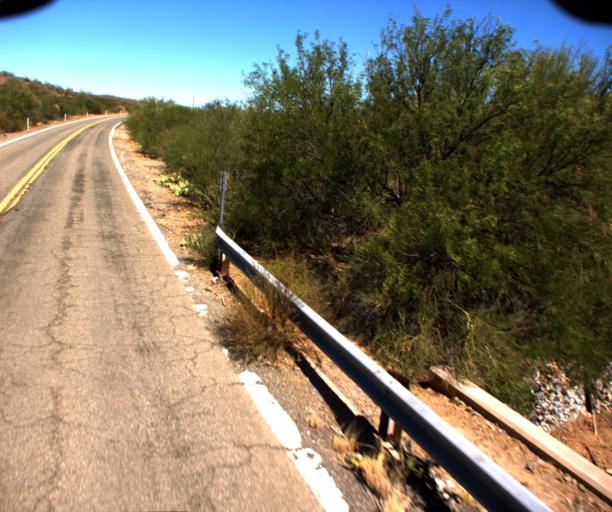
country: US
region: Arizona
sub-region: Pima County
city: Sells
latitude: 32.1709
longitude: -112.1496
